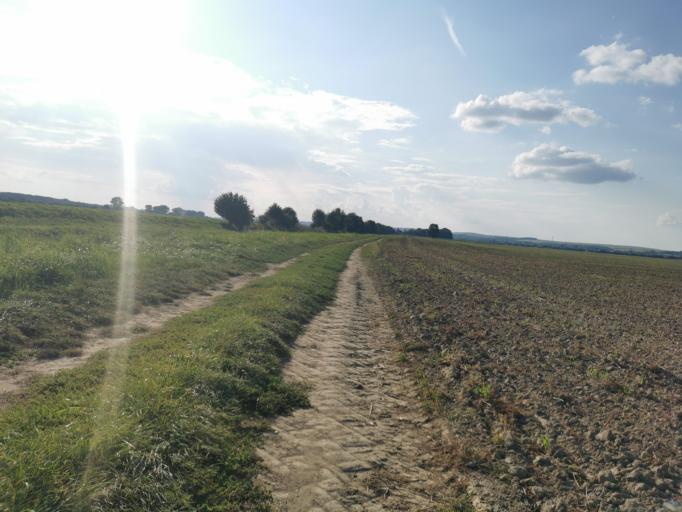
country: SK
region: Trnavsky
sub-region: Okres Senica
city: Senica
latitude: 48.6675
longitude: 17.2927
